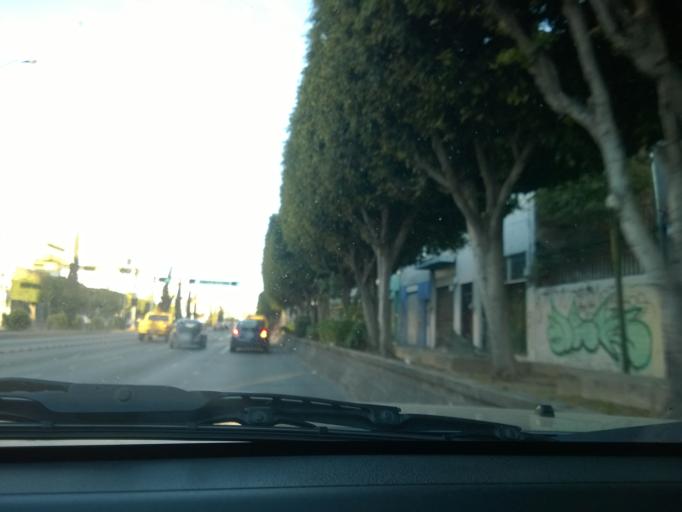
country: MX
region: Guanajuato
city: Leon
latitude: 21.1239
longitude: -101.6774
